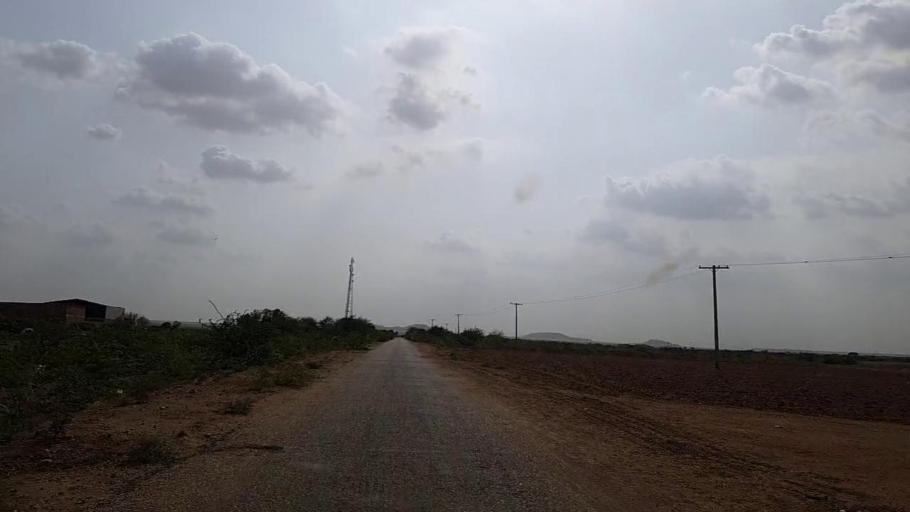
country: PK
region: Sindh
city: Kotri
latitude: 25.2525
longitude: 68.2345
